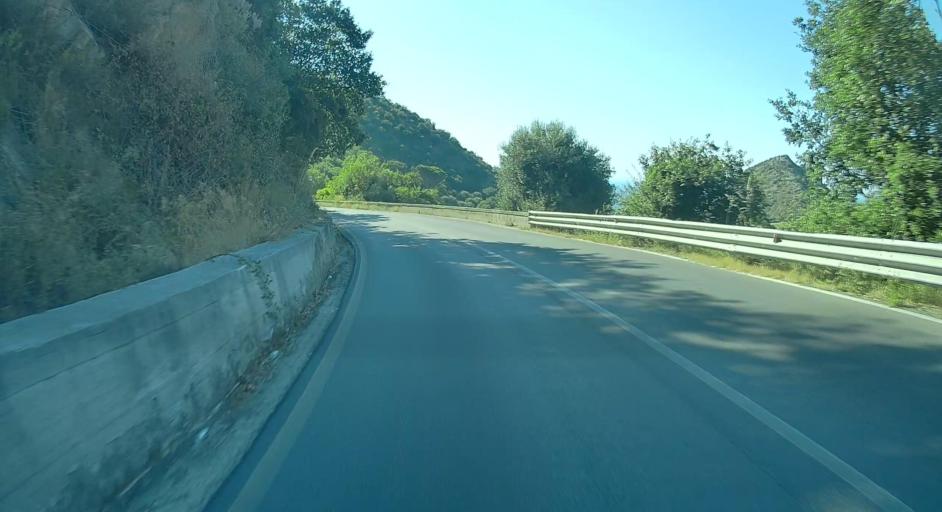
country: IT
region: Sicily
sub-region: Messina
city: Oliveri
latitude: 38.1388
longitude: 15.0323
